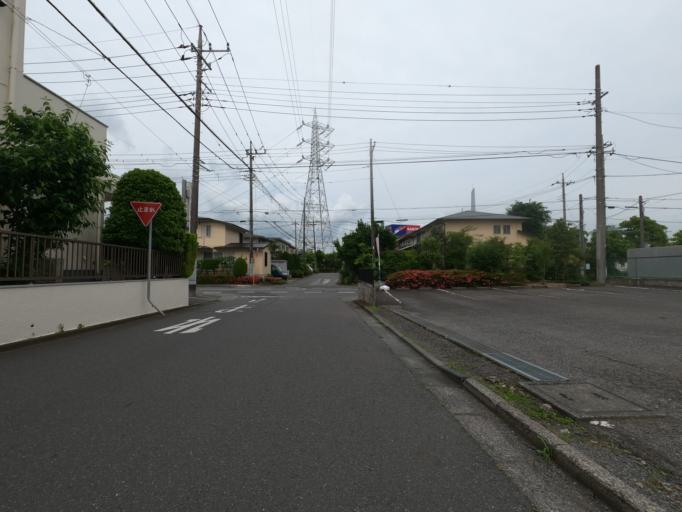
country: JP
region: Ibaraki
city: Moriya
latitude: 35.9664
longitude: 139.9768
